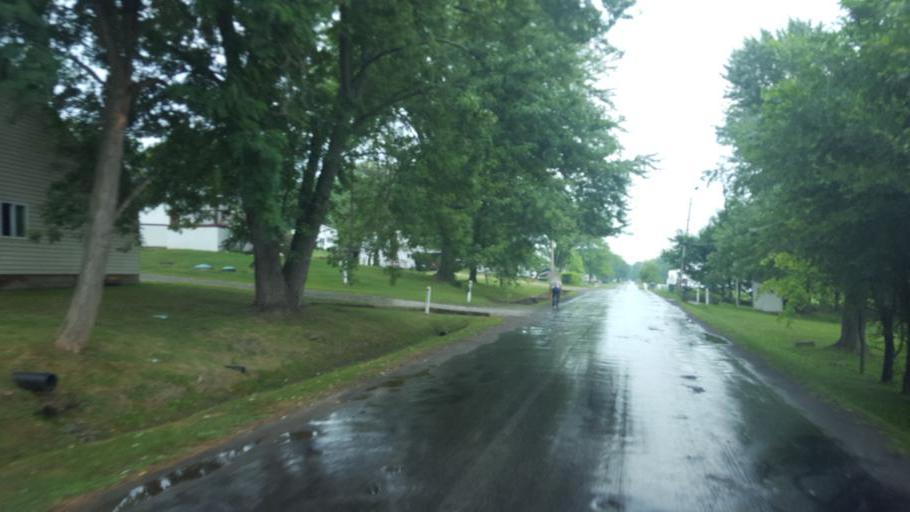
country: US
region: Ohio
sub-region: Geauga County
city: Middlefield
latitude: 41.4394
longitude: -80.9944
